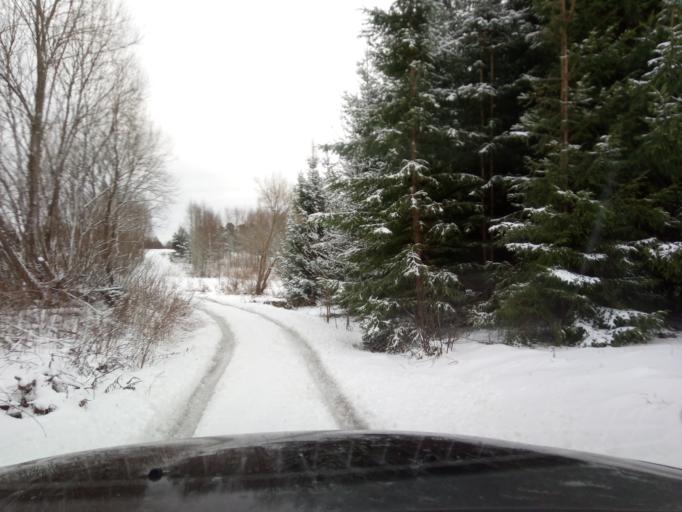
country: LT
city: Zarasai
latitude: 55.6723
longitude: 25.9811
